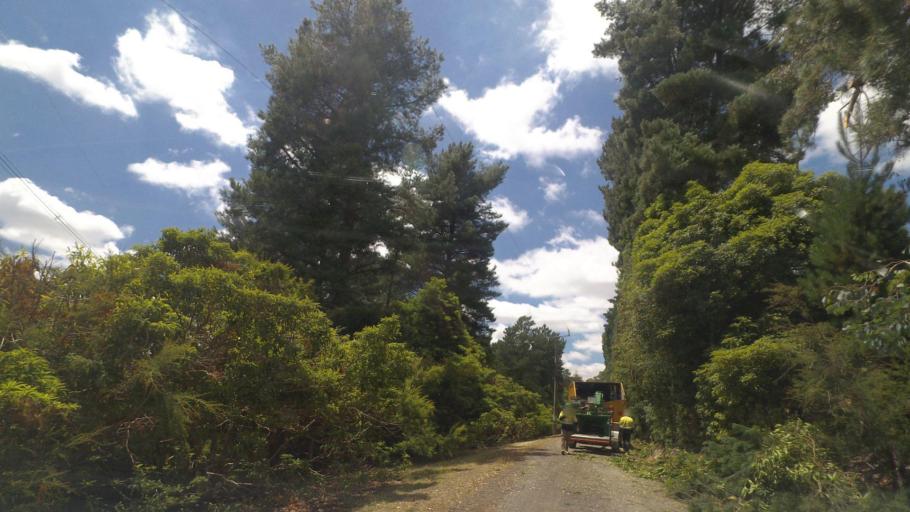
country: AU
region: Victoria
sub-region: Maroondah
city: Croydon Hills
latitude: -37.7507
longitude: 145.2745
